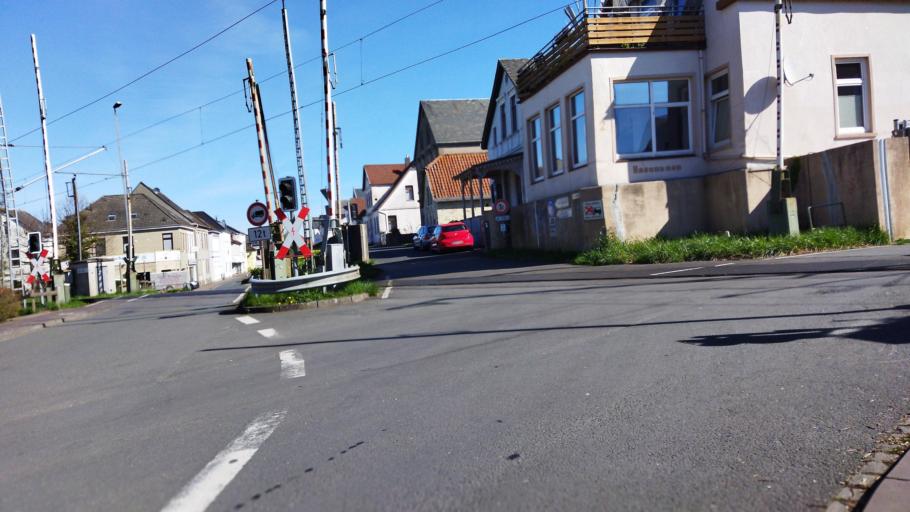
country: DE
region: Lower Saxony
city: Elsfleth
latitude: 53.2365
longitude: 8.4640
